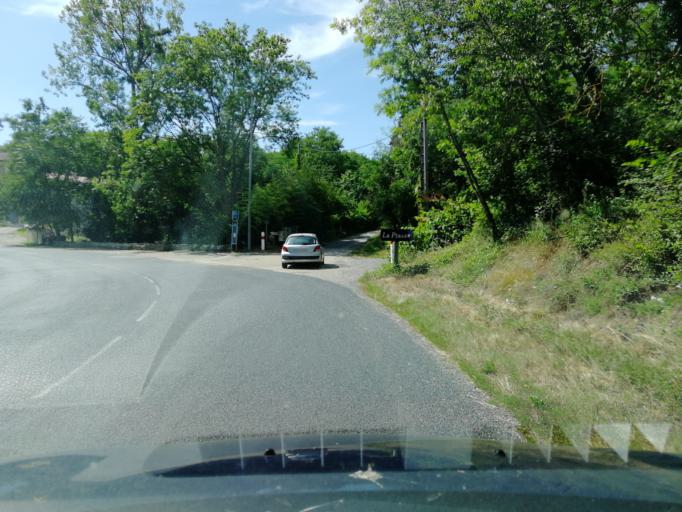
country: FR
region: Rhone-Alpes
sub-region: Departement du Rhone
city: Mornant
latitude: 45.6292
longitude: 4.6545
